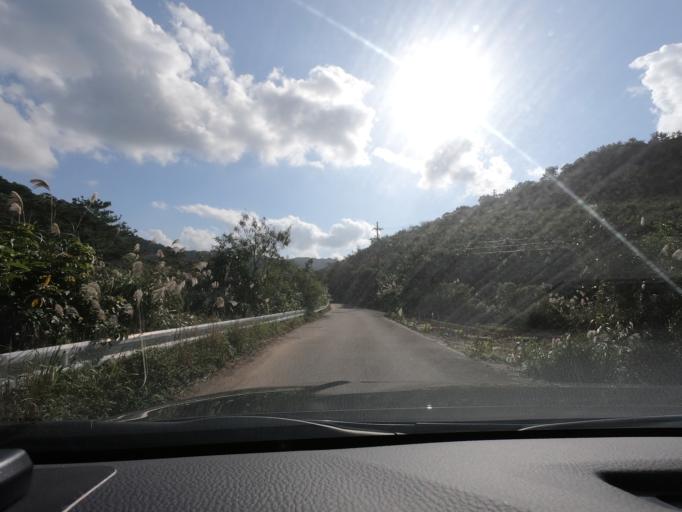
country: JP
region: Okinawa
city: Nago
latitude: 26.7660
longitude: 128.2097
